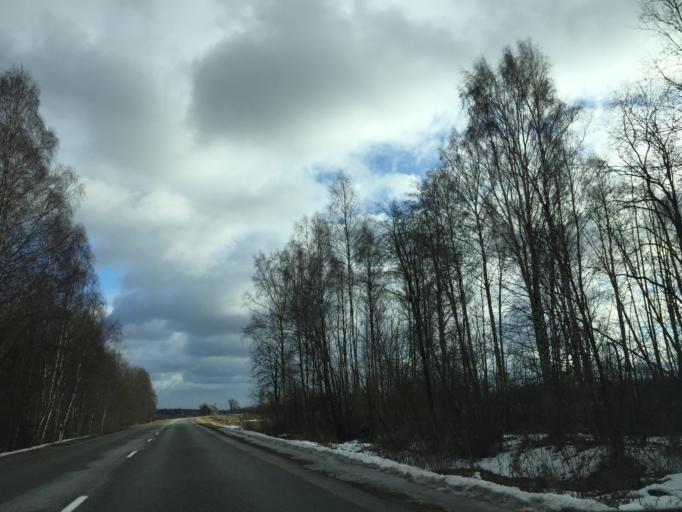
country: LV
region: Aloja
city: Staicele
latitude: 57.8752
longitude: 24.6744
